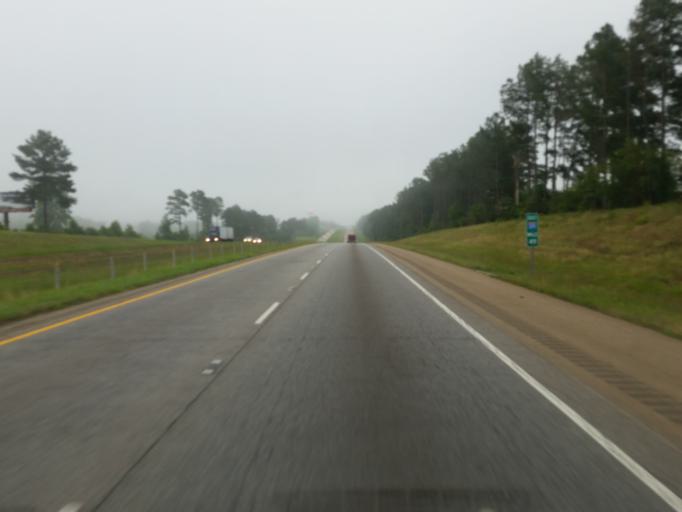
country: US
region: Louisiana
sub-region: Webster Parish
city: Minden
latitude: 32.5840
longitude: -93.2658
